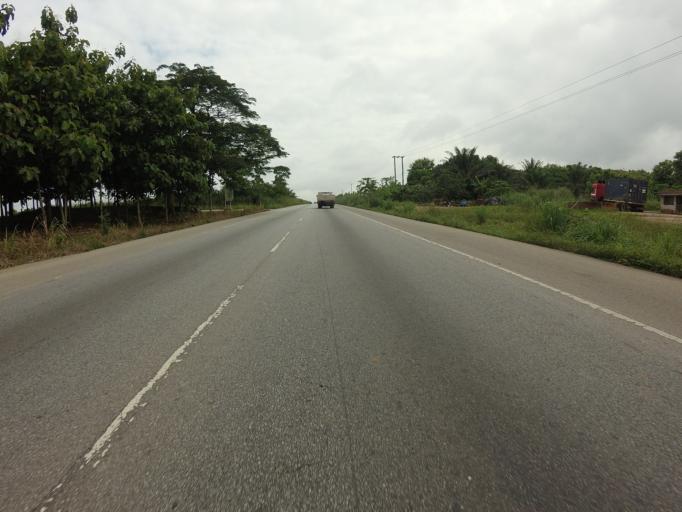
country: GH
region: Ashanti
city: Tafo
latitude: 6.9779
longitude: -1.6866
